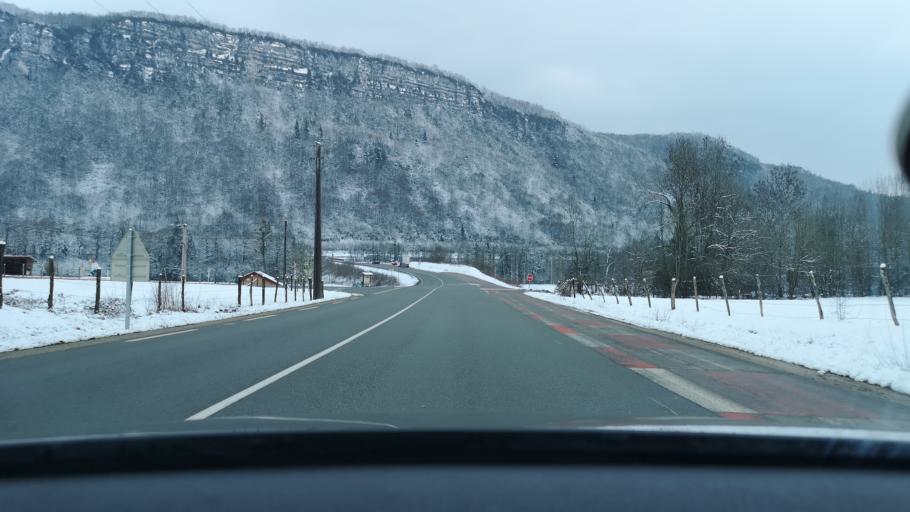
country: FR
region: Rhone-Alpes
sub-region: Departement de l'Ain
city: Dortan
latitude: 46.3662
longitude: 5.7048
